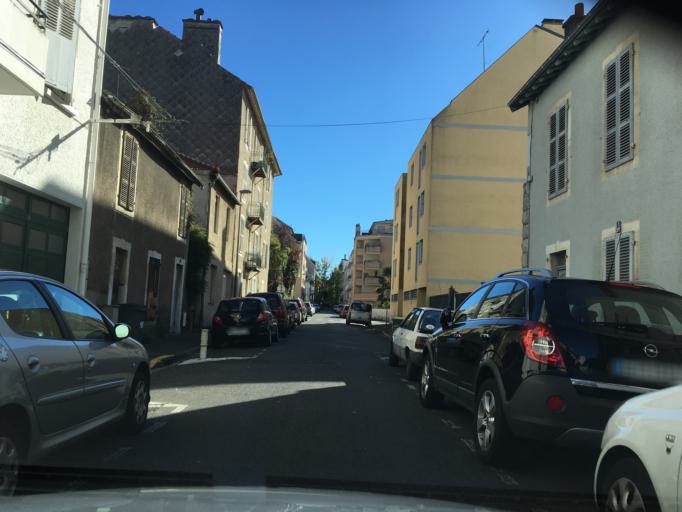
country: FR
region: Aquitaine
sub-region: Departement des Pyrenees-Atlantiques
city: Pau
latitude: 43.3037
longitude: -0.3630
